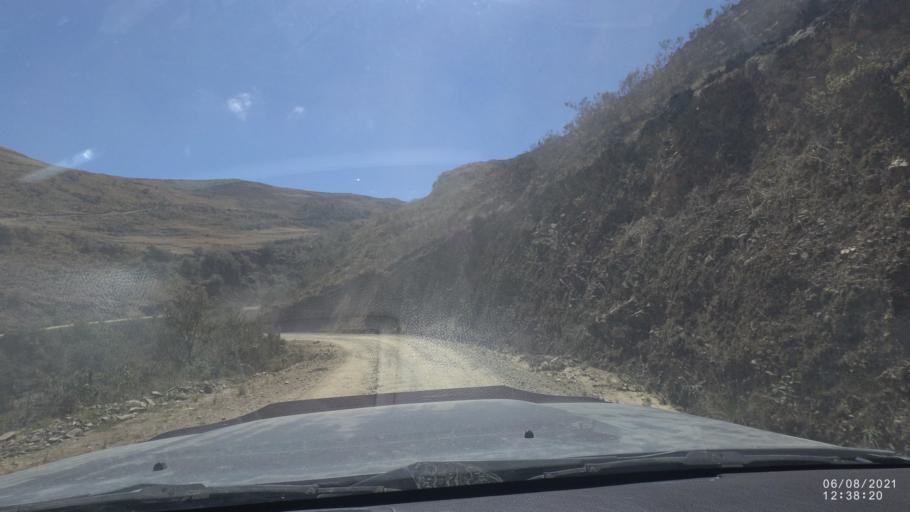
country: BO
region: Cochabamba
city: Colchani
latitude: -16.7779
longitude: -66.6613
